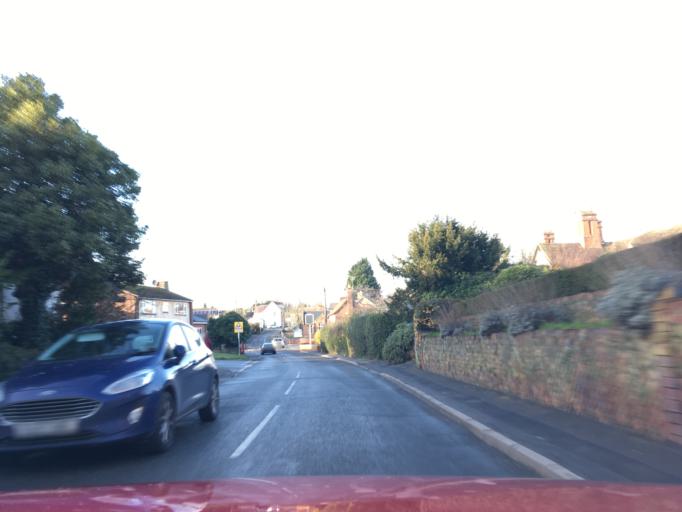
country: GB
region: England
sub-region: Warwickshire
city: Stratford-upon-Avon
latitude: 52.2360
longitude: -1.6882
